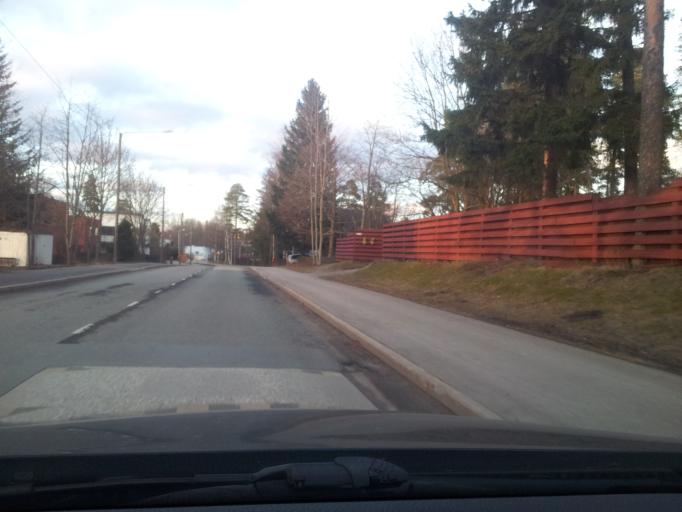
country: FI
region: Uusimaa
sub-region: Helsinki
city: Koukkuniemi
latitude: 60.1754
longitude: 24.7677
